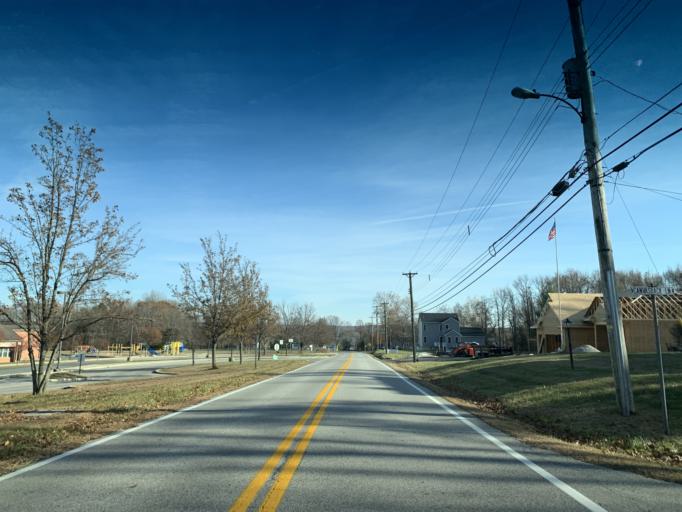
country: US
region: Maryland
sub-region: Cecil County
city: Charlestown
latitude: 39.5739
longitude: -75.9835
